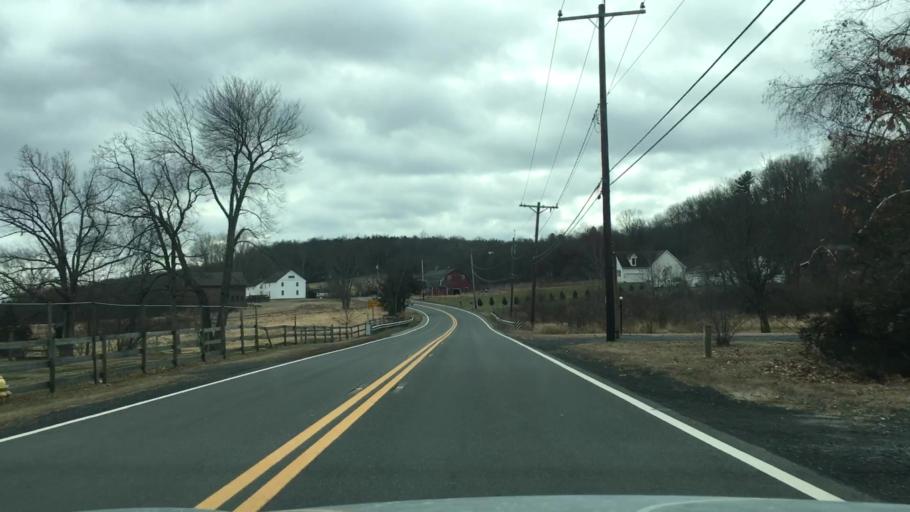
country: US
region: Connecticut
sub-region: Hartford County
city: North Granby
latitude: 42.0145
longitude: -72.7937
